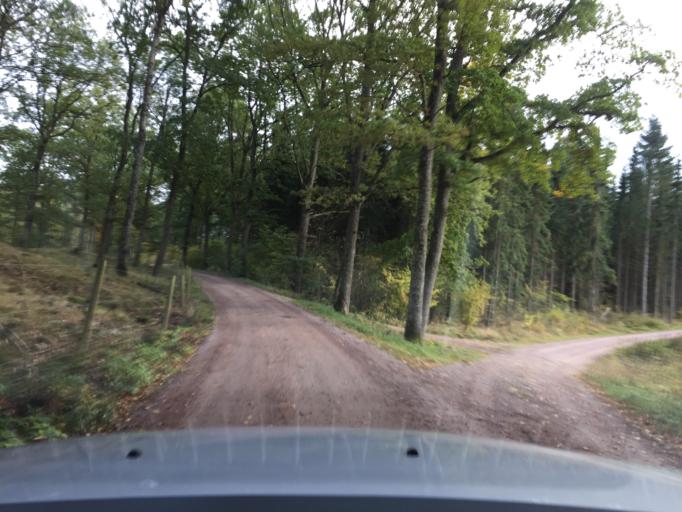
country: SE
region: Skane
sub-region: Hassleholms Kommun
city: Tormestorp
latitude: 56.0528
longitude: 13.7292
